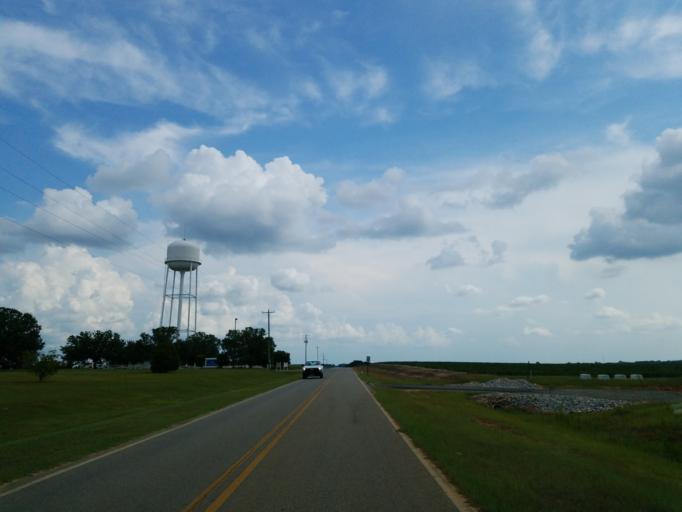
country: US
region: Georgia
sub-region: Dooly County
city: Unadilla
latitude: 32.2820
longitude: -83.7188
